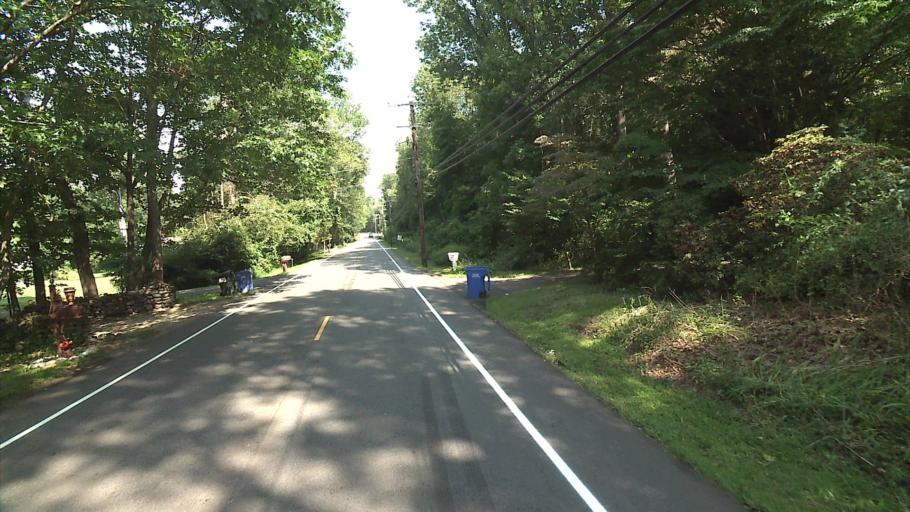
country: US
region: Connecticut
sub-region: New Haven County
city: Madison Center
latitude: 41.3116
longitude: -72.6063
